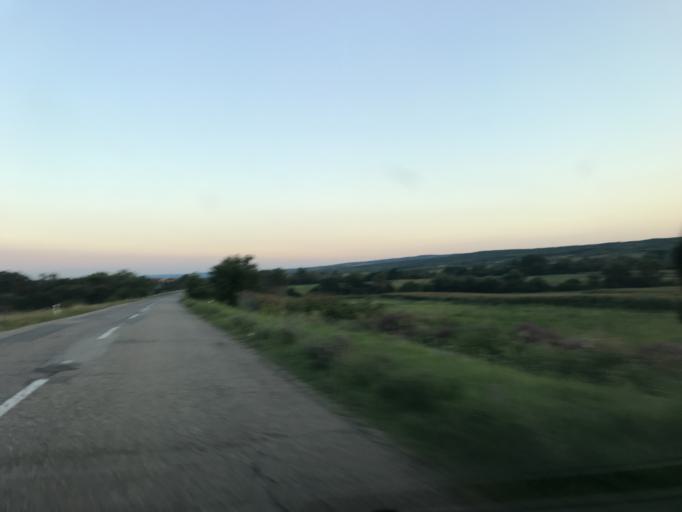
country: RO
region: Mehedinti
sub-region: Comuna Gogosu
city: Ostrovu Mare
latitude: 44.3020
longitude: 22.5069
